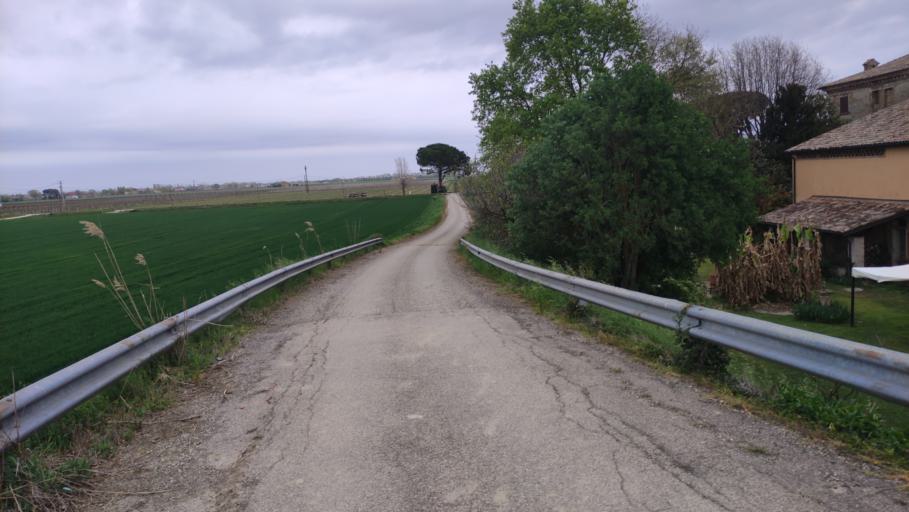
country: IT
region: Emilia-Romagna
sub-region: Provincia di Ravenna
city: Godo
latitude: 44.4023
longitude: 12.0539
